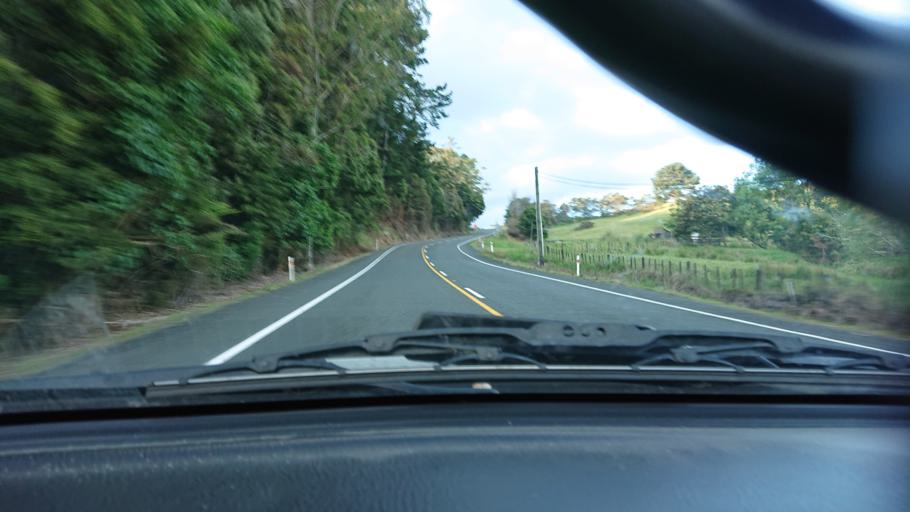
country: NZ
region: Auckland
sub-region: Auckland
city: Parakai
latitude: -36.5275
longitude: 174.4543
